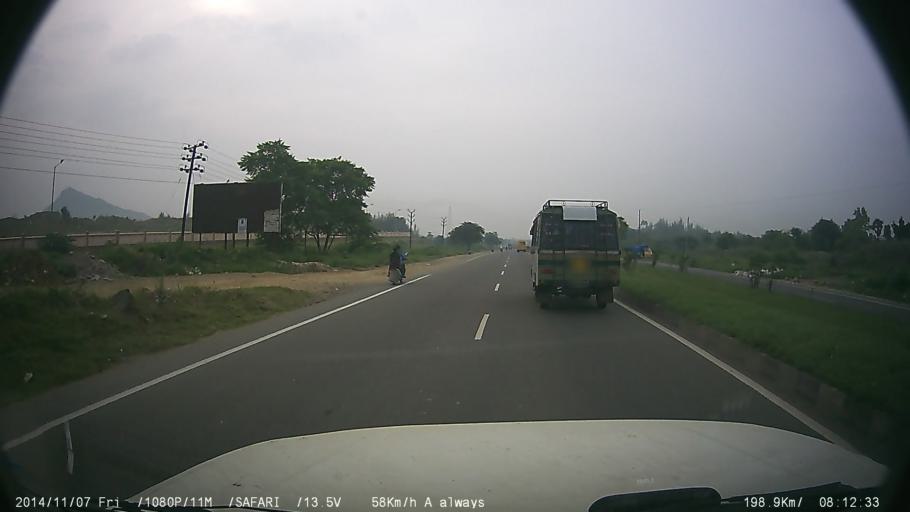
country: IN
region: Tamil Nadu
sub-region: Salem
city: Salem
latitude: 11.6997
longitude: 78.1051
